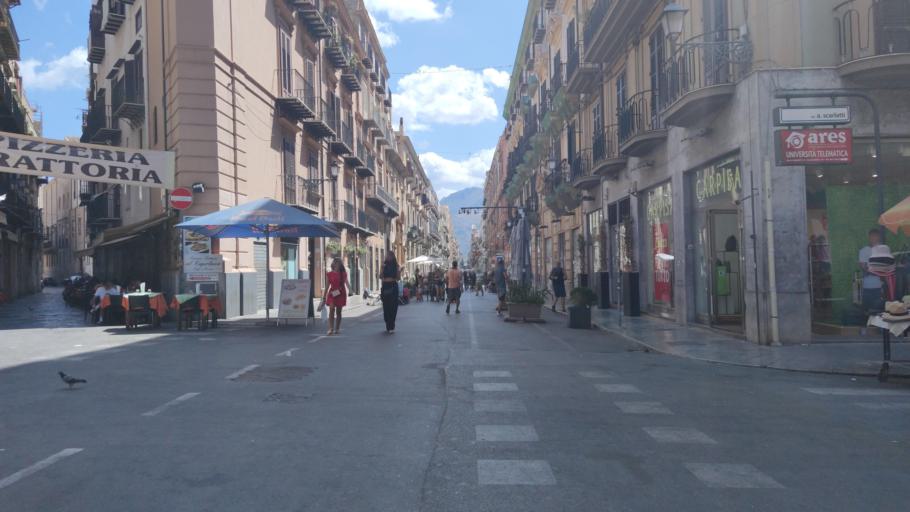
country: IT
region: Sicily
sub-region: Palermo
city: Palermo
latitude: 38.1198
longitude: 13.3589
